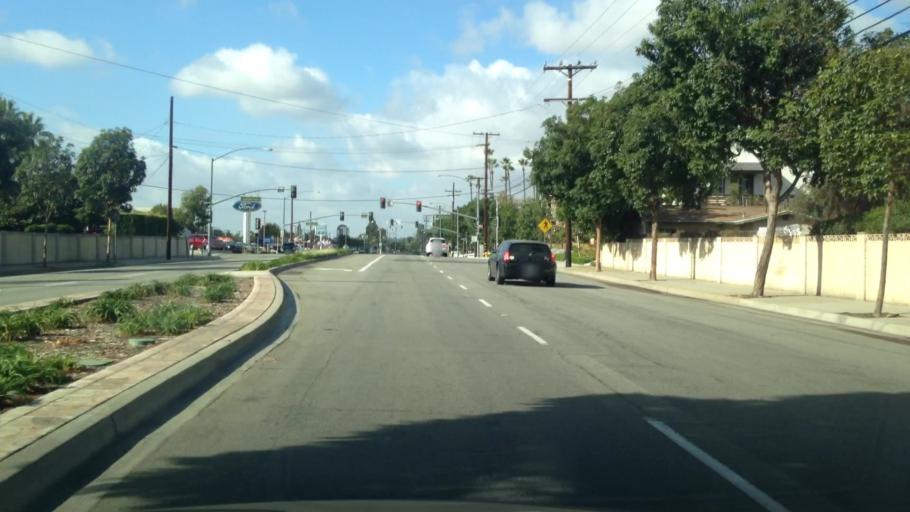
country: US
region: California
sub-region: Orange County
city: Yorba Linda
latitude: 33.8885
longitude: -117.8362
